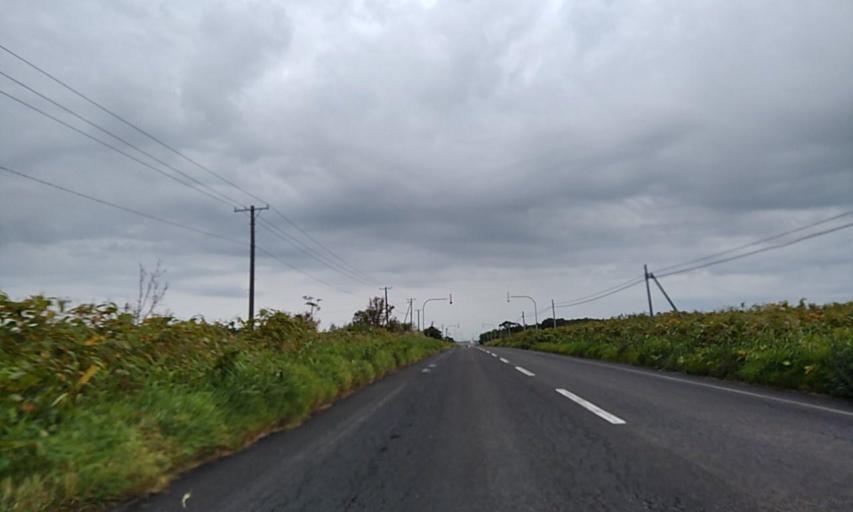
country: JP
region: Hokkaido
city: Nayoro
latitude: 44.6503
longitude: 142.8876
